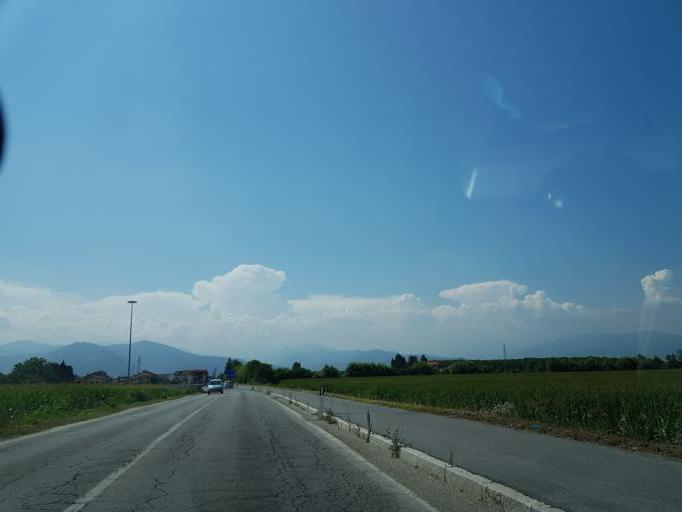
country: IT
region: Piedmont
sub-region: Provincia di Cuneo
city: San Defendente
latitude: 44.3948
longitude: 7.5145
